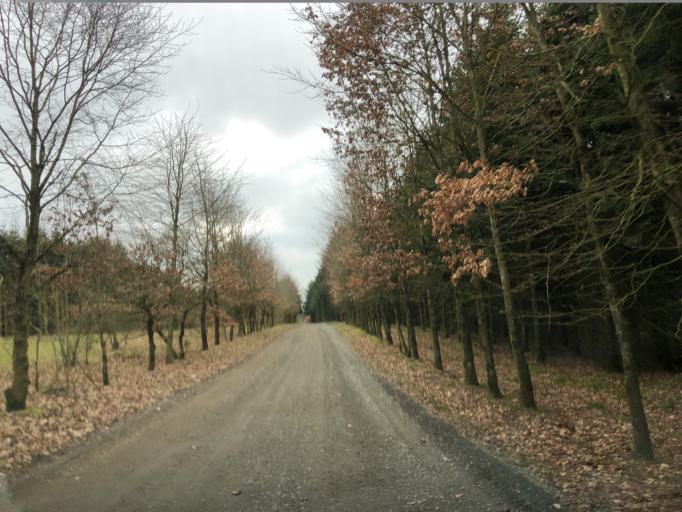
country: DK
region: South Denmark
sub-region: Billund Kommune
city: Billund
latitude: 55.7798
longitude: 9.1774
